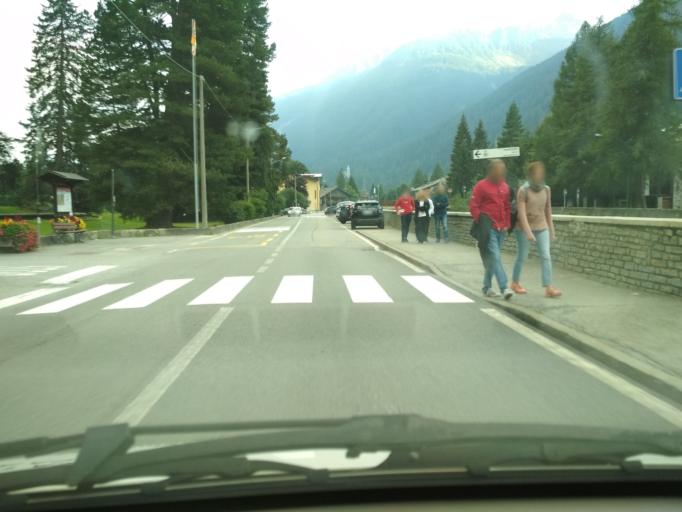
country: IT
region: Aosta Valley
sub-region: Valle d'Aosta
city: Gressoney-Saint-Jean
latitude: 45.7774
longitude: 7.8269
